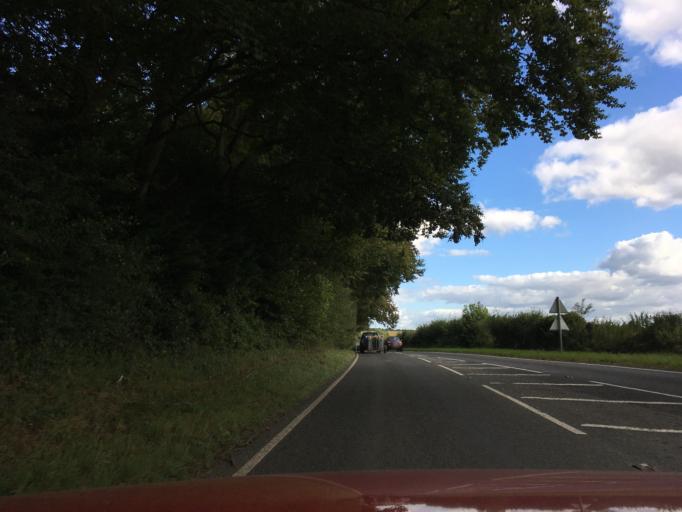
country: GB
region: England
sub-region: Hampshire
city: Chandlers Ford
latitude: 51.1020
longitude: -1.4083
